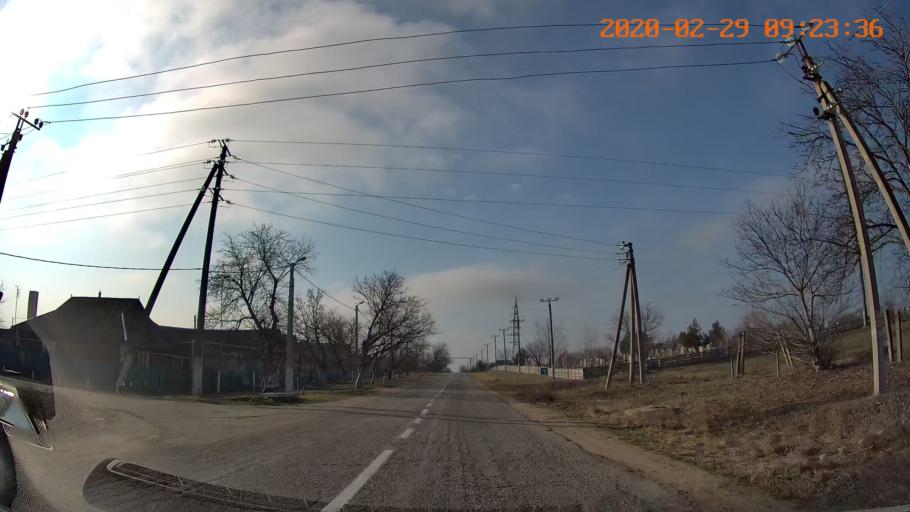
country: MD
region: Telenesti
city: Pervomaisc
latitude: 46.7241
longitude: 29.9608
